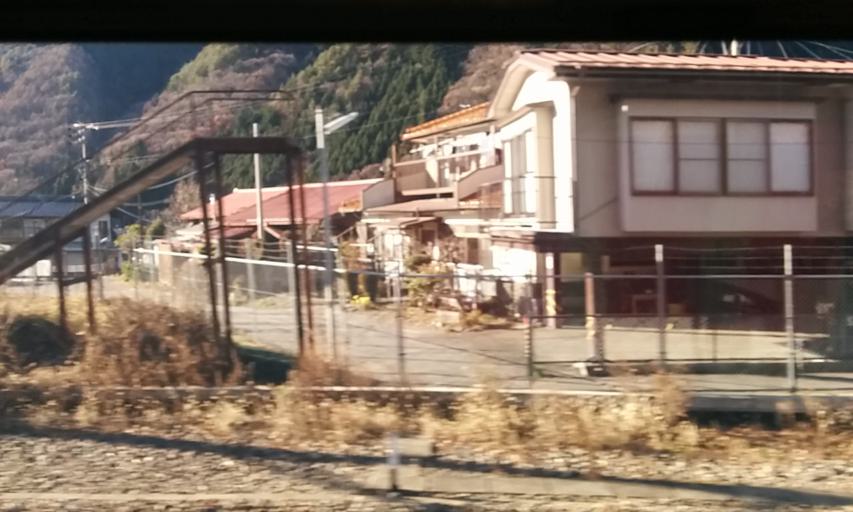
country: JP
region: Nagano
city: Ina
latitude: 35.8468
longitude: 137.6953
